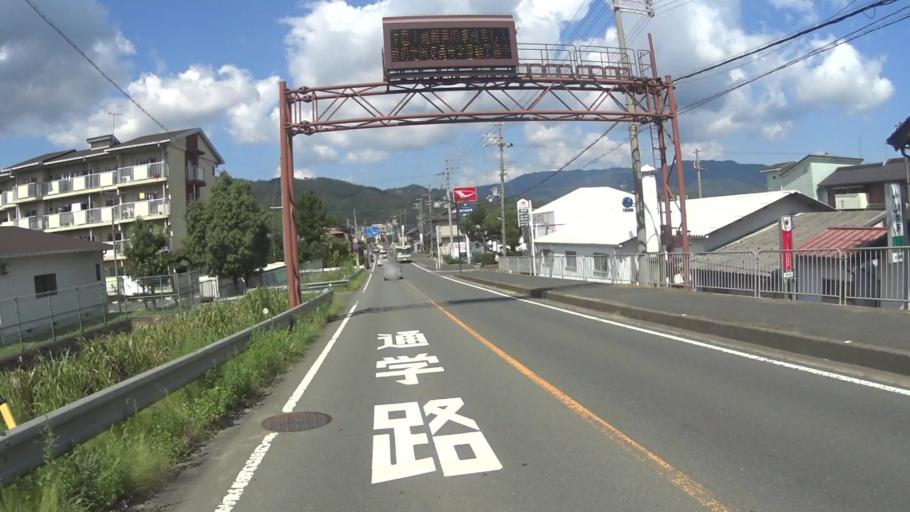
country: JP
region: Kyoto
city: Miyazu
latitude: 35.5603
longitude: 135.1535
